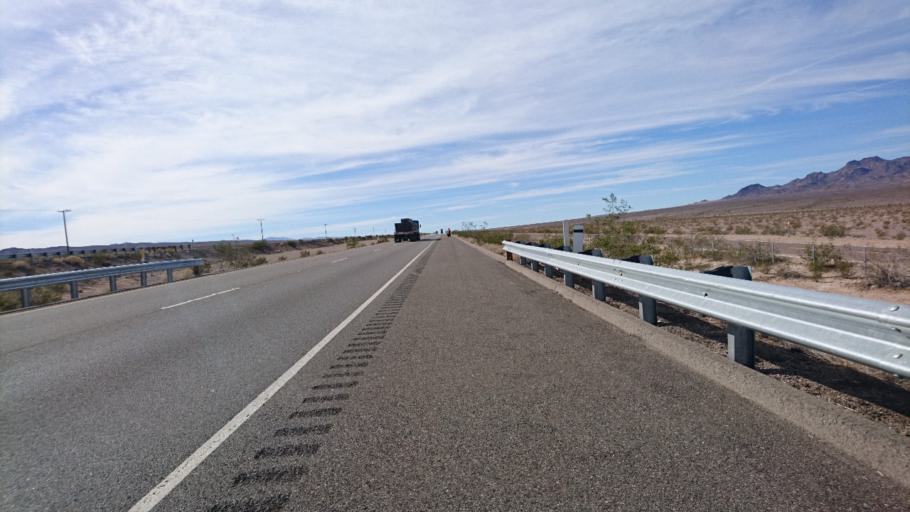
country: US
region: California
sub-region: San Bernardino County
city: Joshua Tree
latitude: 34.7248
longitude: -116.2082
